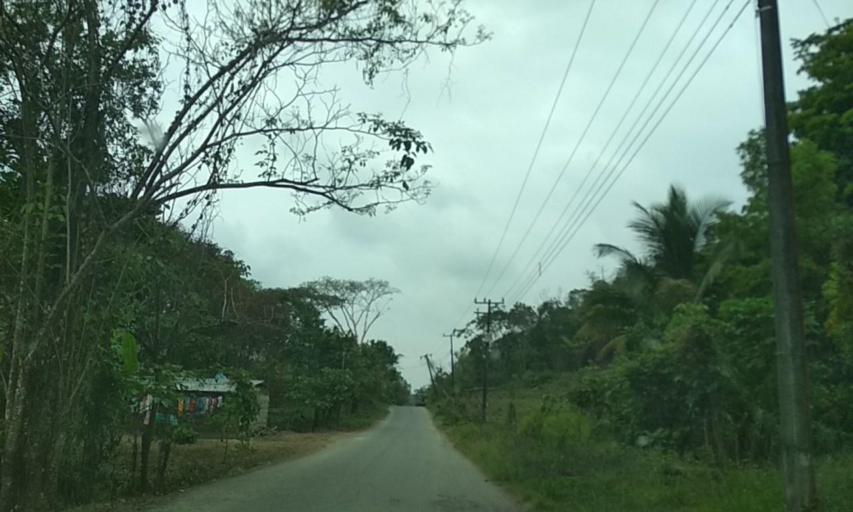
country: MX
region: Veracruz
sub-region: Uxpanapa
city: Poblado 10
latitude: 17.4617
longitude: -94.1059
